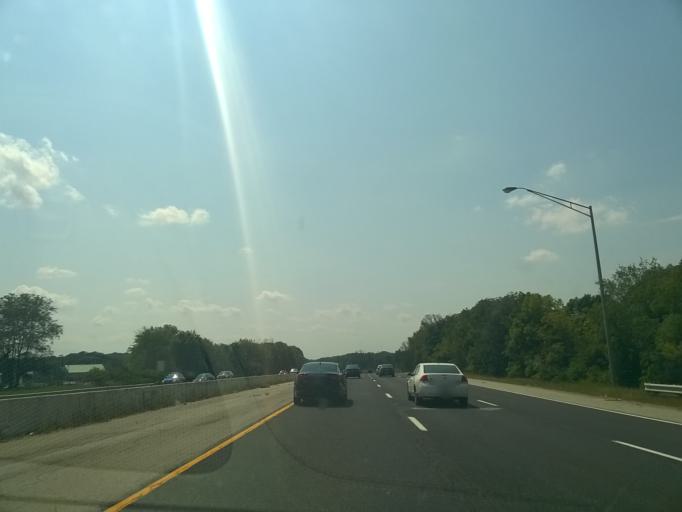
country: US
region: Indiana
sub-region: Boone County
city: Zionsville
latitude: 39.9241
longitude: -86.2688
